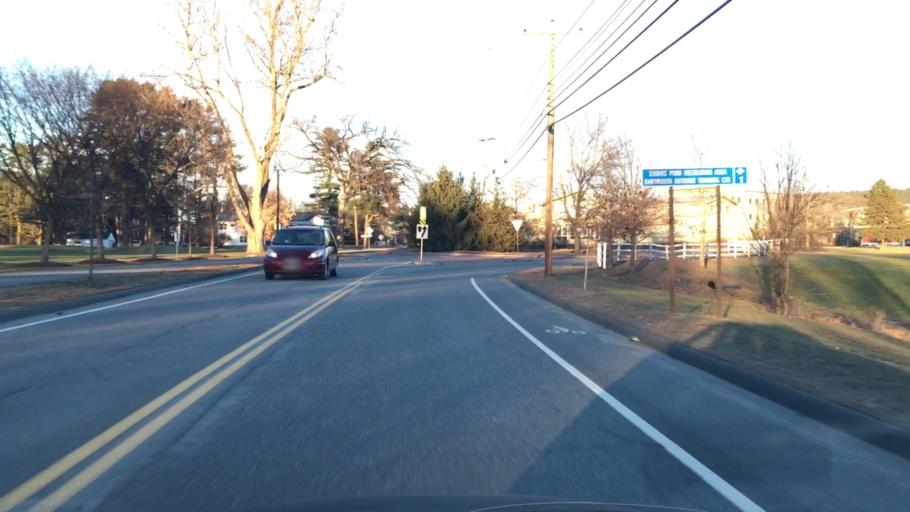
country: US
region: New Hampshire
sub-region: Grafton County
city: Hanover
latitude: 43.7176
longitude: -72.2747
